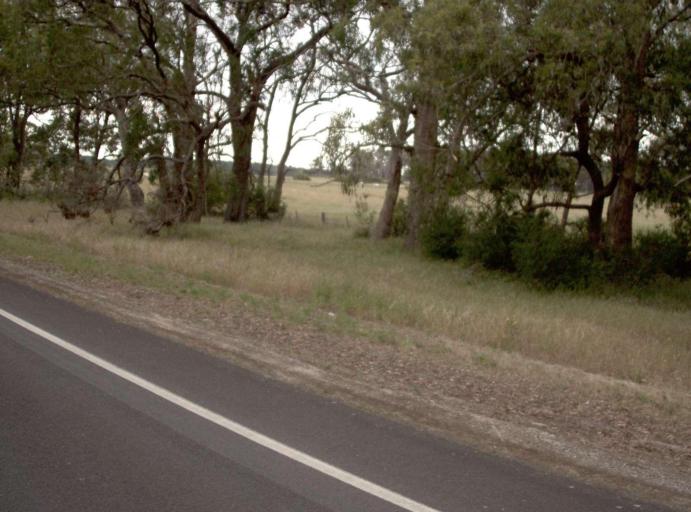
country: AU
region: Victoria
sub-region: Wellington
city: Sale
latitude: -38.3082
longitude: 147.0297
